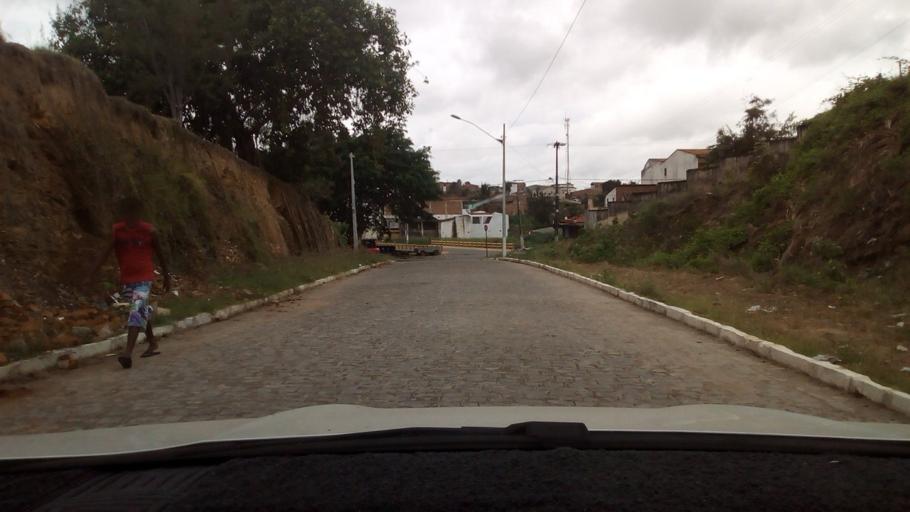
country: BR
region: Paraiba
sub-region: Guarabira
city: Guarabira
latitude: -6.8557
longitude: -35.4865
